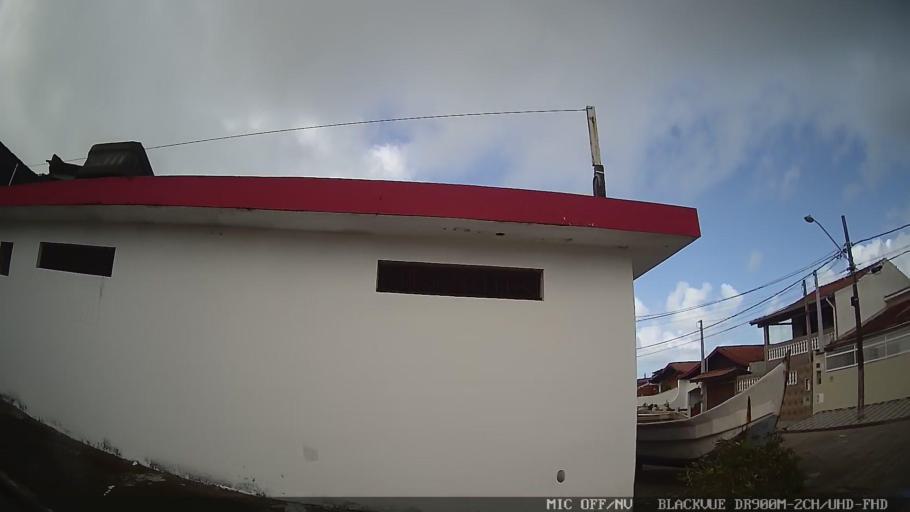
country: BR
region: Sao Paulo
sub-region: Itanhaem
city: Itanhaem
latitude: -24.1563
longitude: -46.7353
